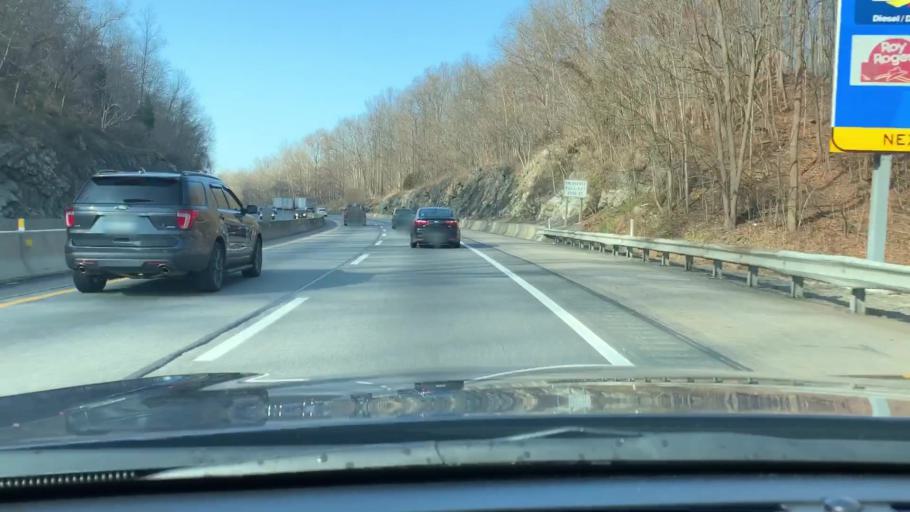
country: US
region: Pennsylvania
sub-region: Chester County
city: Downingtown
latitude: 40.0959
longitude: -75.7358
